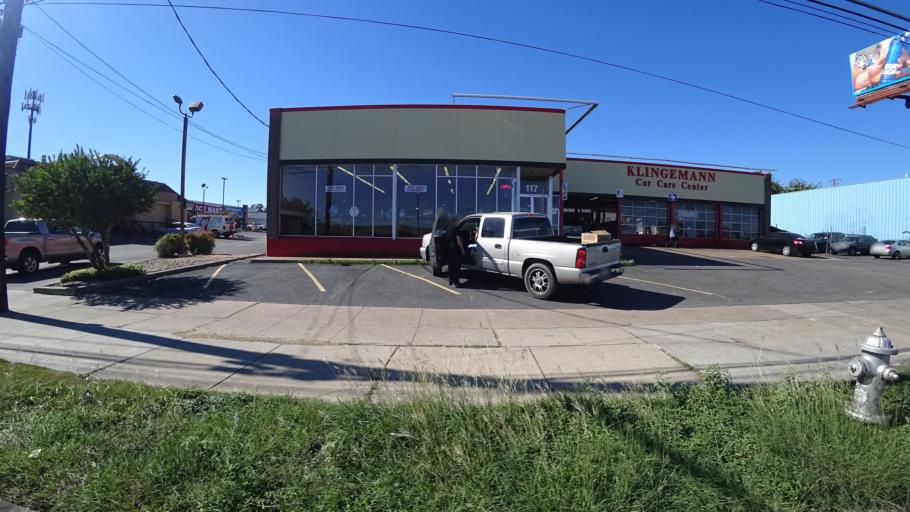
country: US
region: Texas
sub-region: Travis County
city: Austin
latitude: 30.2382
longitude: -97.7527
